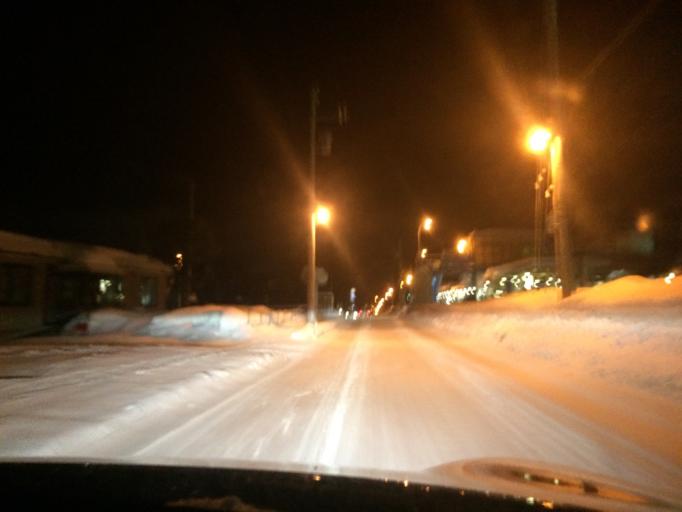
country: JP
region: Hokkaido
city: Ebetsu
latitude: 43.0450
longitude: 141.4622
